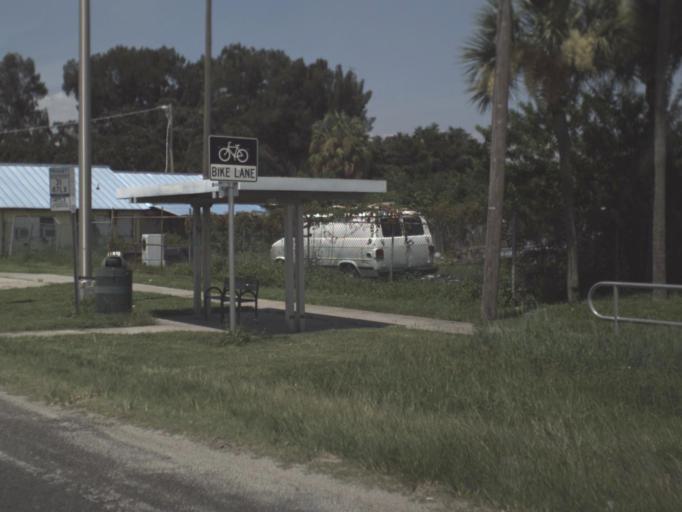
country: US
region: Florida
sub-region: Hillsborough County
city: Gibsonton
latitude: 27.8415
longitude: -82.3816
